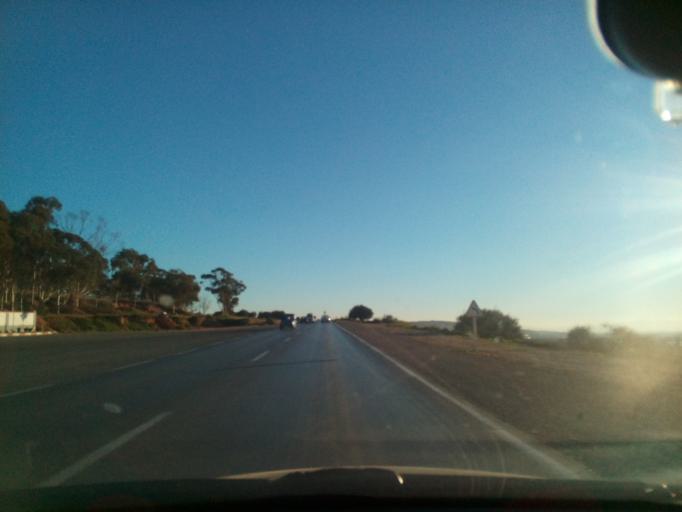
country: DZ
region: Mostaganem
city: Mostaganem
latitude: 35.7675
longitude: 0.1999
